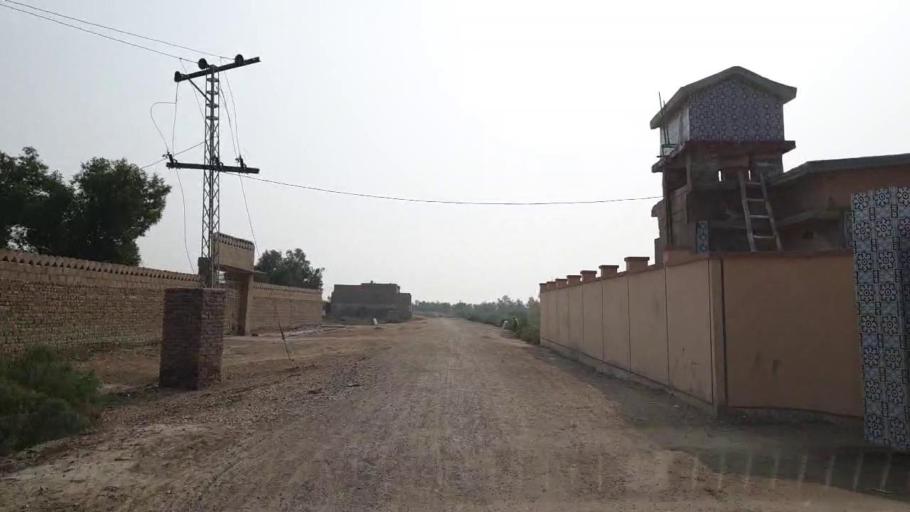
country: PK
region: Sindh
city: Bhan
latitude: 26.5089
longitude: 67.6734
